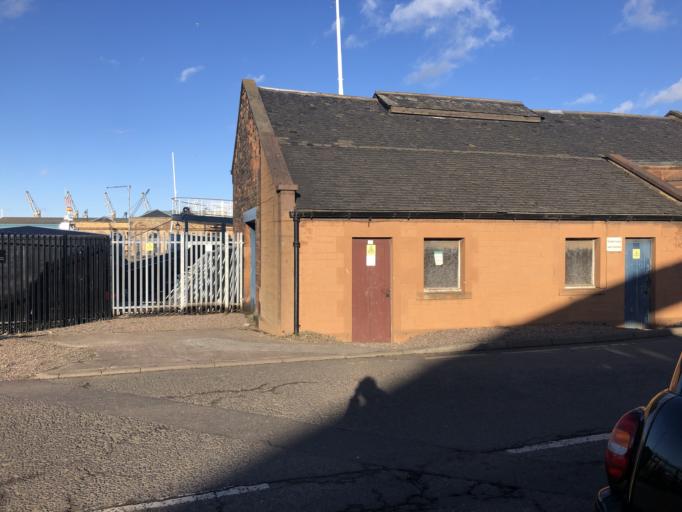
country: GB
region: Scotland
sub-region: West Lothian
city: Seafield
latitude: 55.9789
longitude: -3.1698
